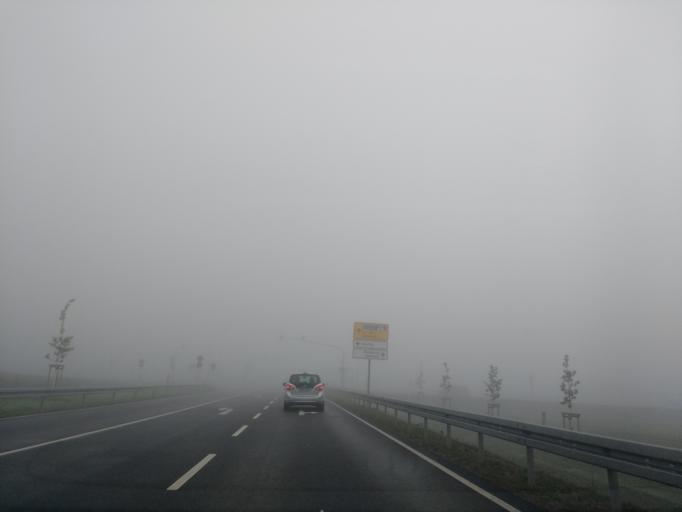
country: DE
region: Saxony-Anhalt
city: Halle (Saale)
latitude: 51.4896
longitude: 12.0173
